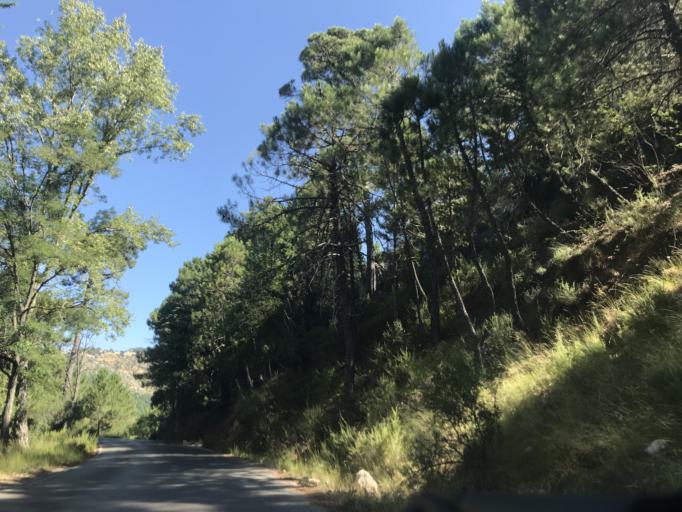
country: ES
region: Andalusia
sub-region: Provincia de Jaen
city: La Iruela
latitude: 37.9189
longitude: -2.9459
